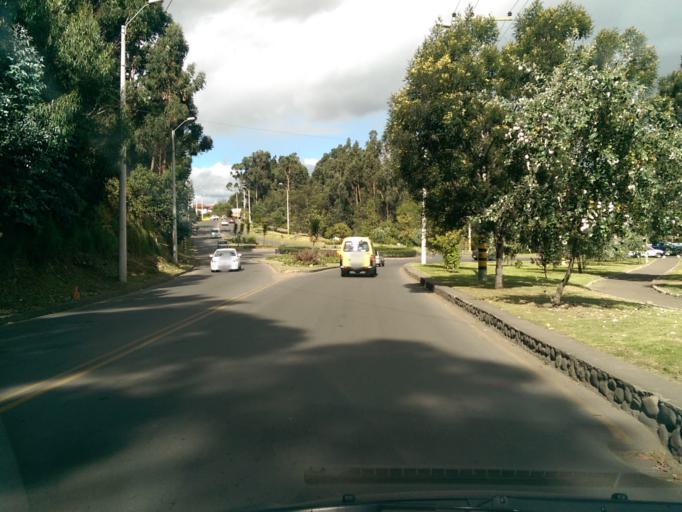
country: EC
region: Azuay
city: Cuenca
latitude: -2.9084
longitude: -79.0195
